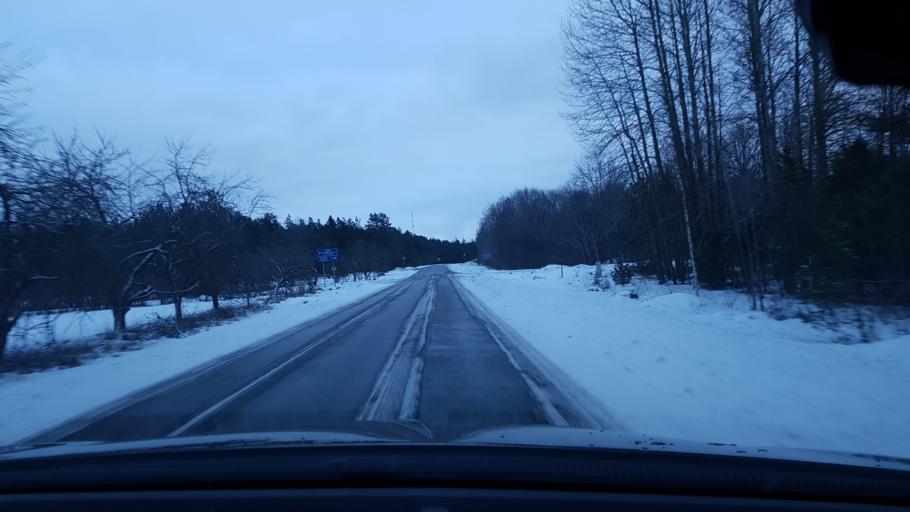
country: EE
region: Laeaene
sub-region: Ridala Parish
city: Uuemoisa
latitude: 59.0690
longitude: 23.5815
